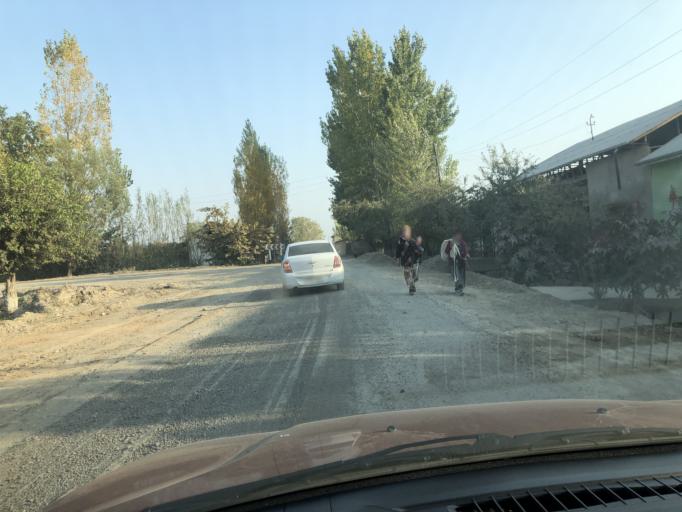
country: UZ
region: Namangan
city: Uychi
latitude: 41.0643
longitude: 71.9875
